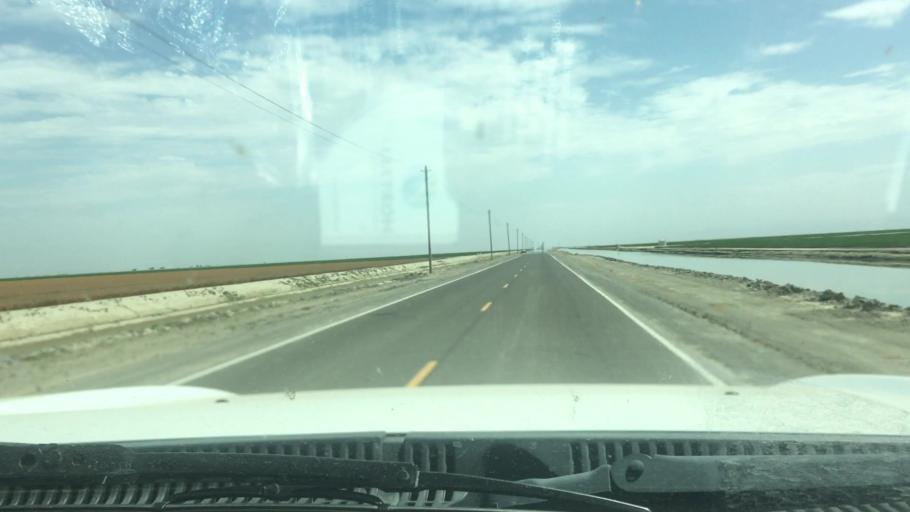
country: US
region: California
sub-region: Tulare County
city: Alpaugh
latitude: 35.9019
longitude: -119.5733
